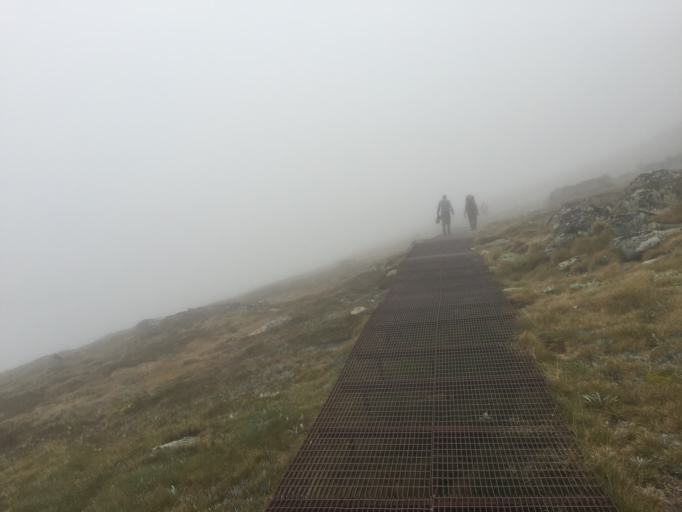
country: AU
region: New South Wales
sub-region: Snowy River
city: Jindabyne
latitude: -36.4629
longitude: 148.2699
